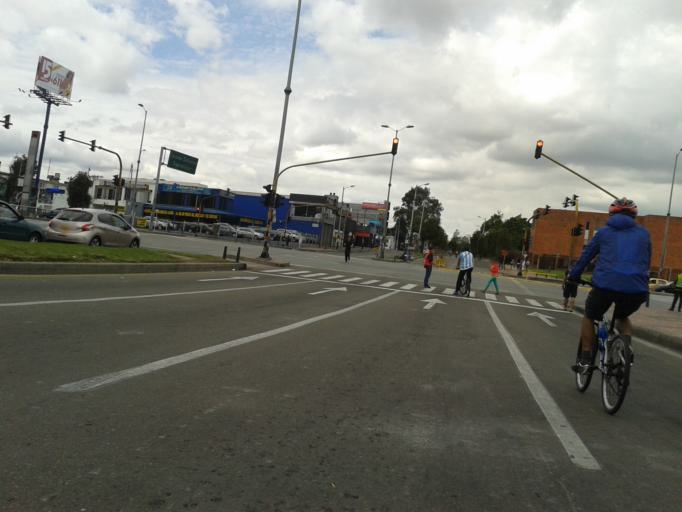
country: CO
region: Bogota D.C.
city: Barrio San Luis
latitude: 4.7003
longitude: -74.0696
